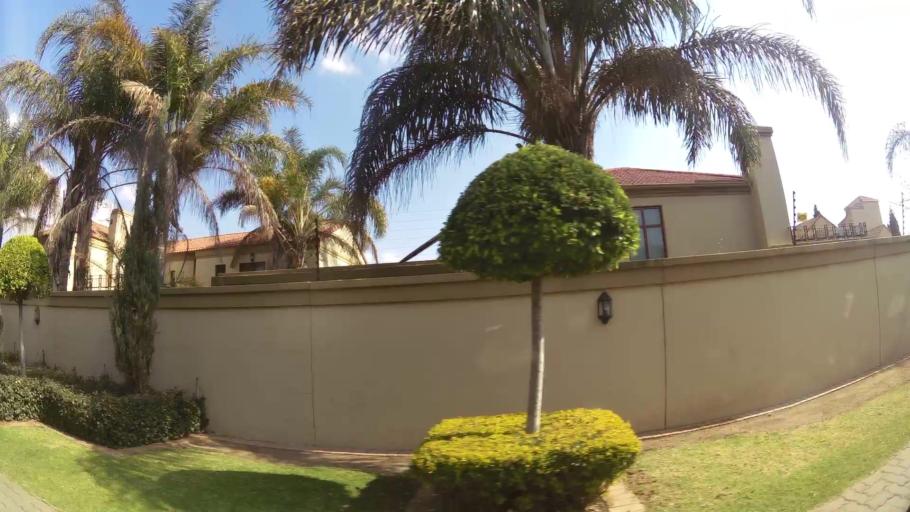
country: ZA
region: Gauteng
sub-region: City of Johannesburg Metropolitan Municipality
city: Midrand
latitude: -26.0270
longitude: 28.0671
